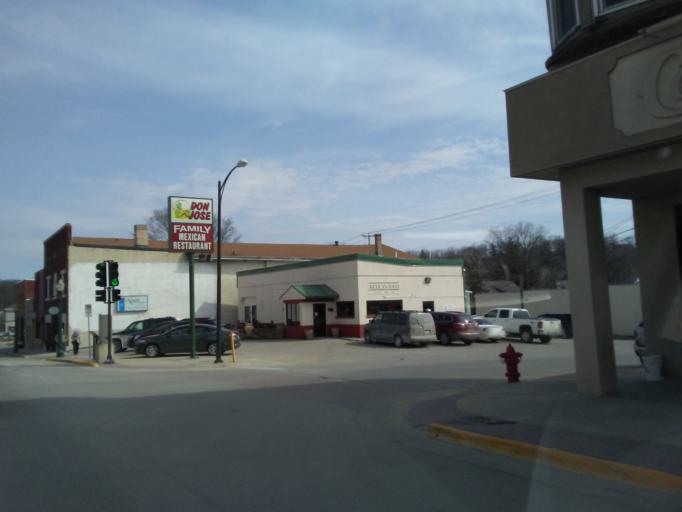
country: US
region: Iowa
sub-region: Winneshiek County
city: Decorah
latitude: 43.3042
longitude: -91.7849
